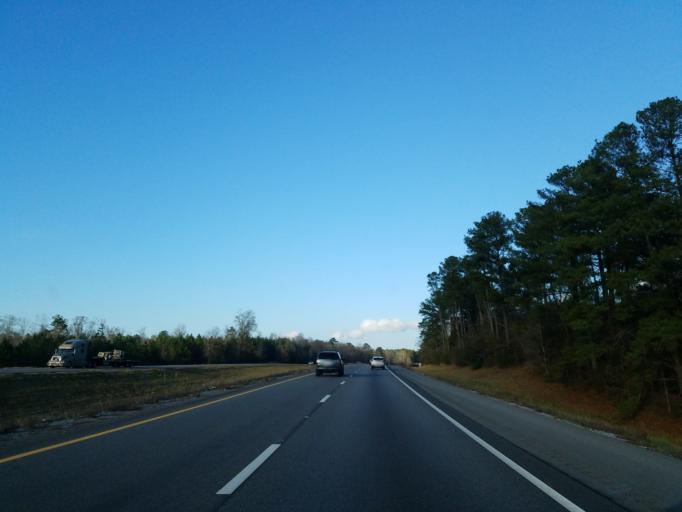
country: US
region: Mississippi
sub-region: Jones County
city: Sharon
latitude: 31.9230
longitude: -89.0033
